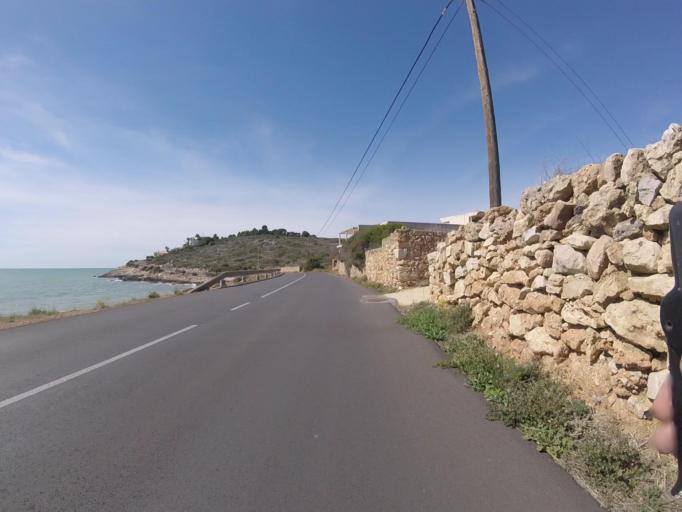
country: ES
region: Valencia
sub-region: Provincia de Castello
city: Peniscola
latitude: 40.3523
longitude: 0.3925
